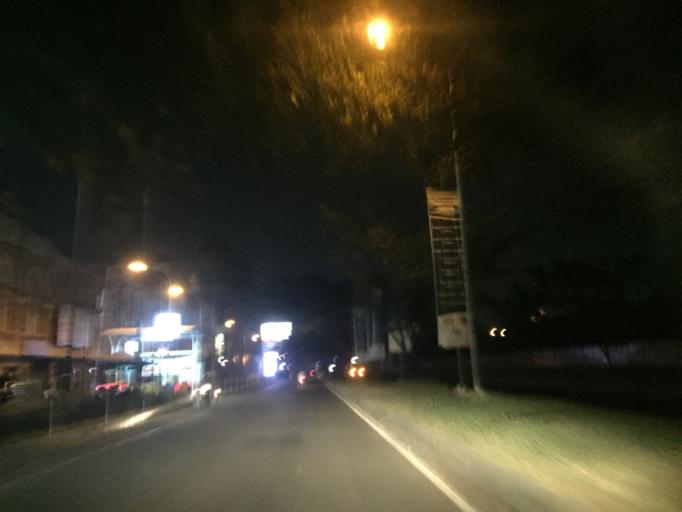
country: ID
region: Banten
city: Tangerang
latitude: -6.2430
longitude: 106.6261
